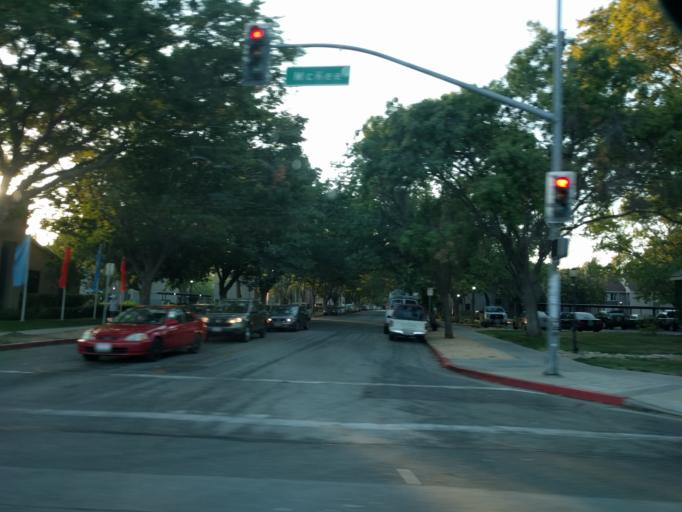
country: US
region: California
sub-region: Santa Clara County
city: Alum Rock
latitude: 37.3600
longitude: -121.8582
